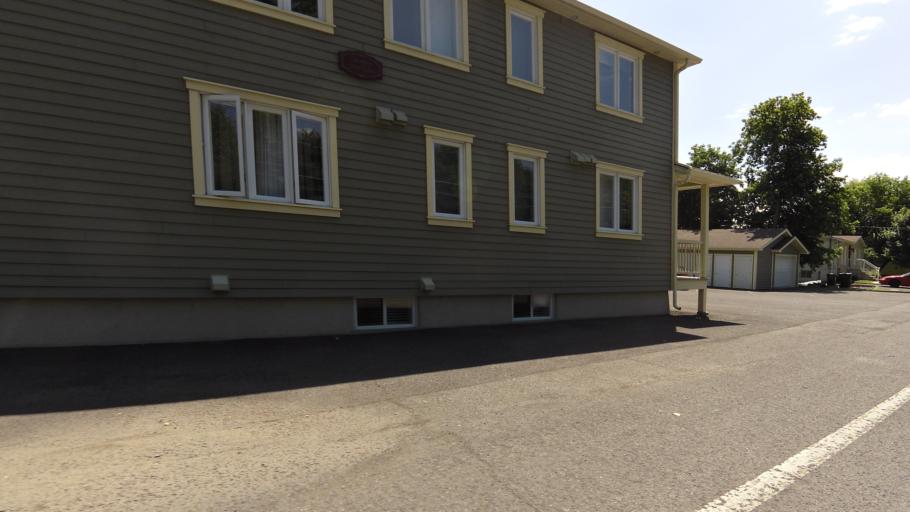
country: CA
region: Quebec
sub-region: Monteregie
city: Saint-Jean-sur-Richelieu
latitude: 45.3533
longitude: -73.2680
